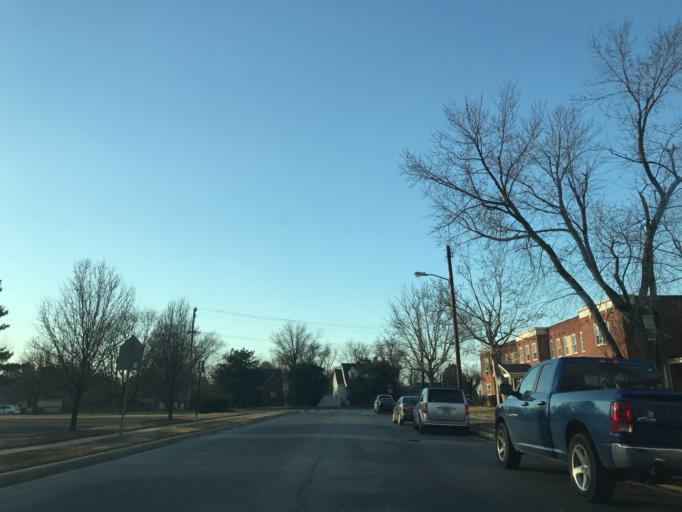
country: US
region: Maryland
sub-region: Baltimore County
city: Dundalk
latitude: 39.2698
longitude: -76.4937
